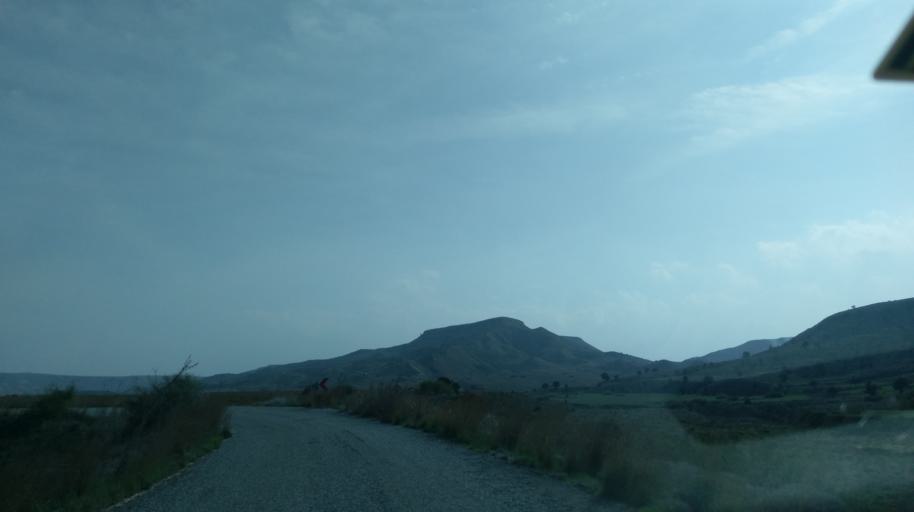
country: CY
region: Lefkosia
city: Morfou
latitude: 35.2490
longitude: 33.0674
